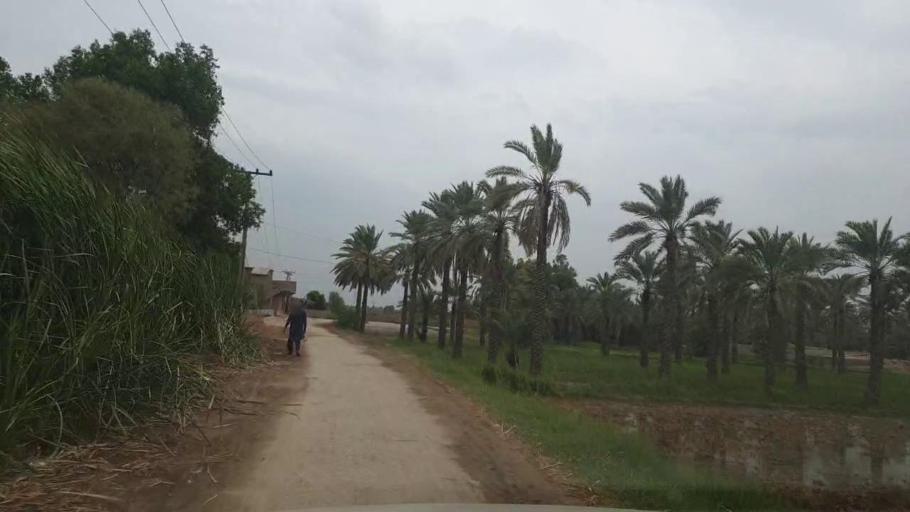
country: PK
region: Sindh
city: Khairpur
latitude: 27.5473
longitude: 68.7394
